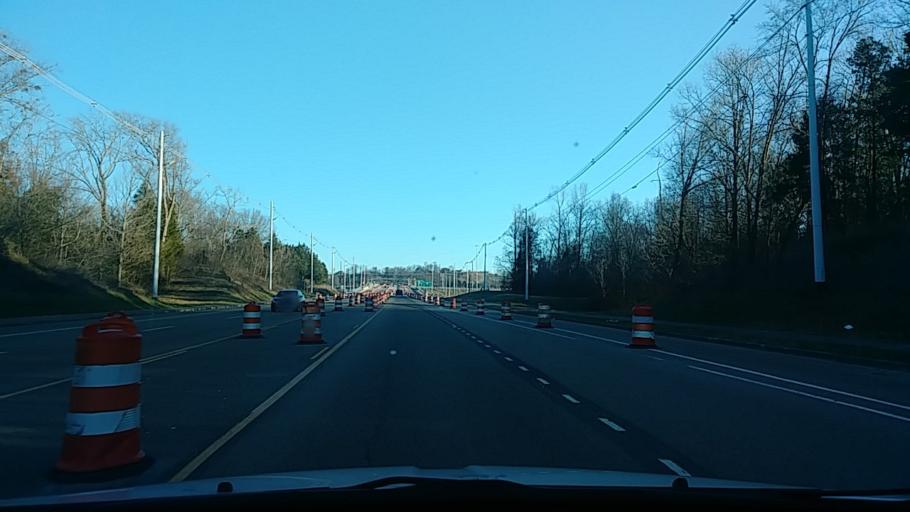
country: US
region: Tennessee
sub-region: Hamblen County
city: Morristown
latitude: 36.1802
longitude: -83.3515
